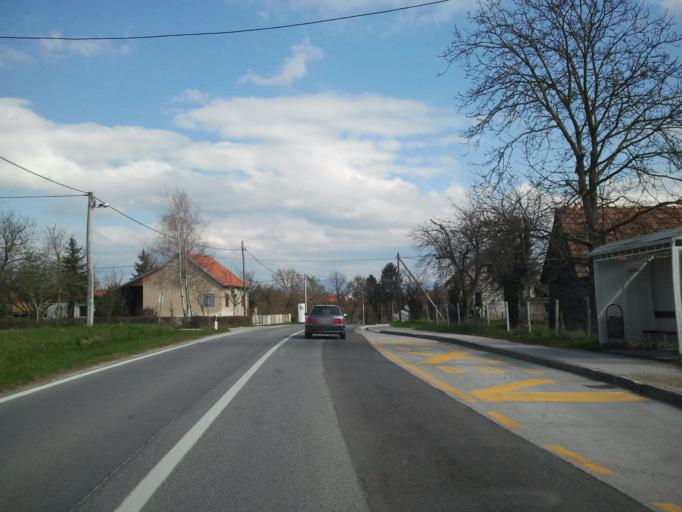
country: HR
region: Karlovacka
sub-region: Grad Karlovac
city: Karlovac
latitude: 45.5790
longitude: 15.5933
